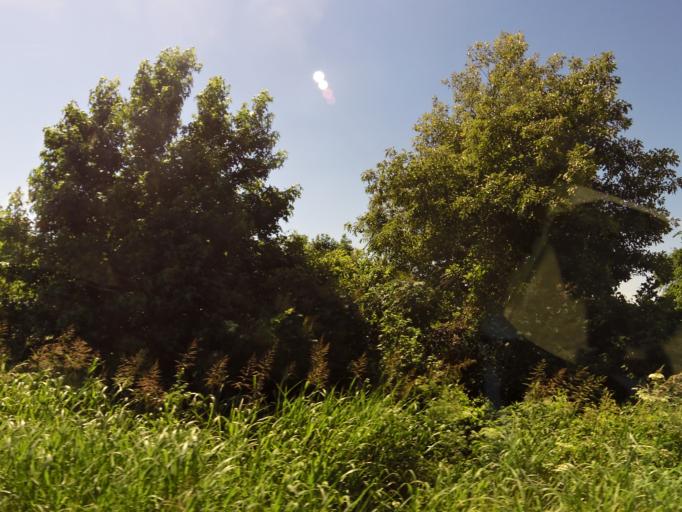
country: US
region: Missouri
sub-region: Dunklin County
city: Campbell
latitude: 36.4617
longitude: -90.1276
